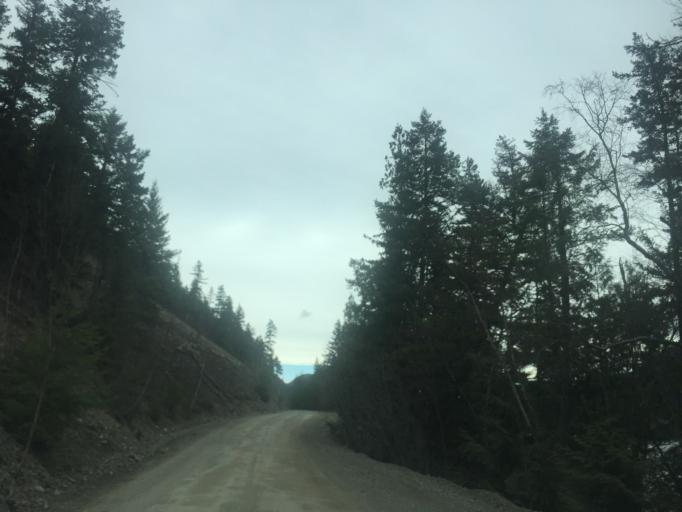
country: CA
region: British Columbia
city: Chase
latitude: 51.4136
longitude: -120.1295
